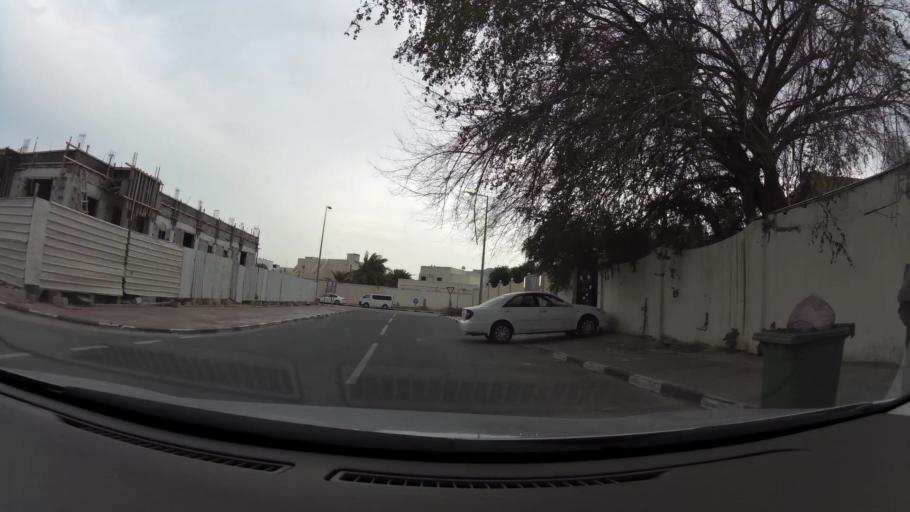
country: QA
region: Baladiyat ad Dawhah
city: Doha
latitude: 25.3410
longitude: 51.5083
